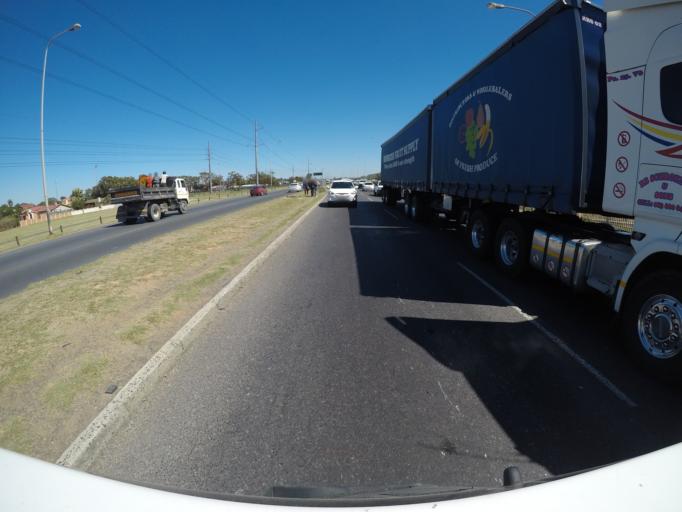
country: ZA
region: Western Cape
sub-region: Cape Winelands District Municipality
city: Stellenbosch
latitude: -34.0883
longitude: 18.8384
